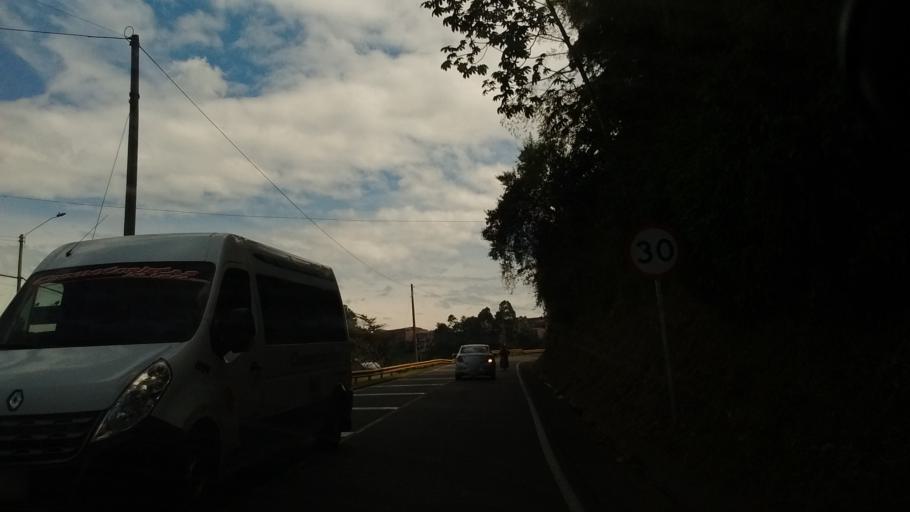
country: CO
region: Cauca
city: Cajibio
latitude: 2.6343
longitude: -76.5282
